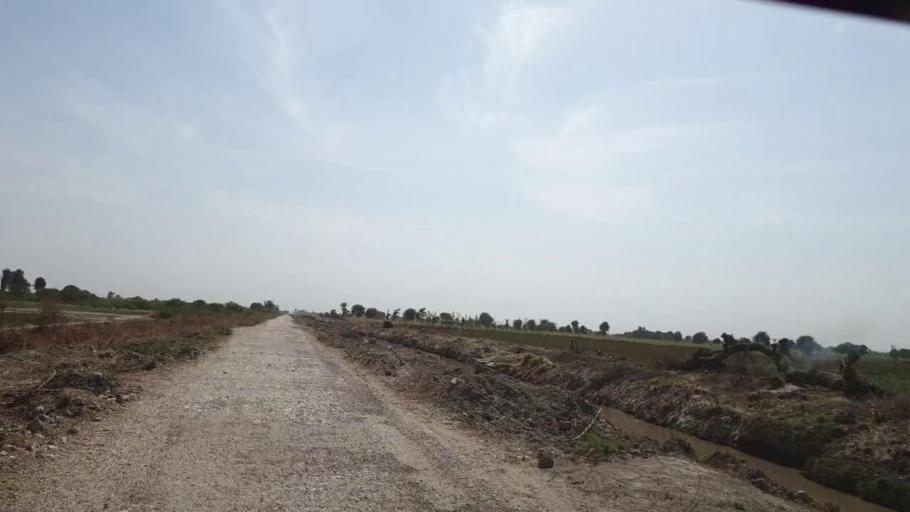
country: PK
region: Sindh
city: Nabisar
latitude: 25.0934
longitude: 69.5815
